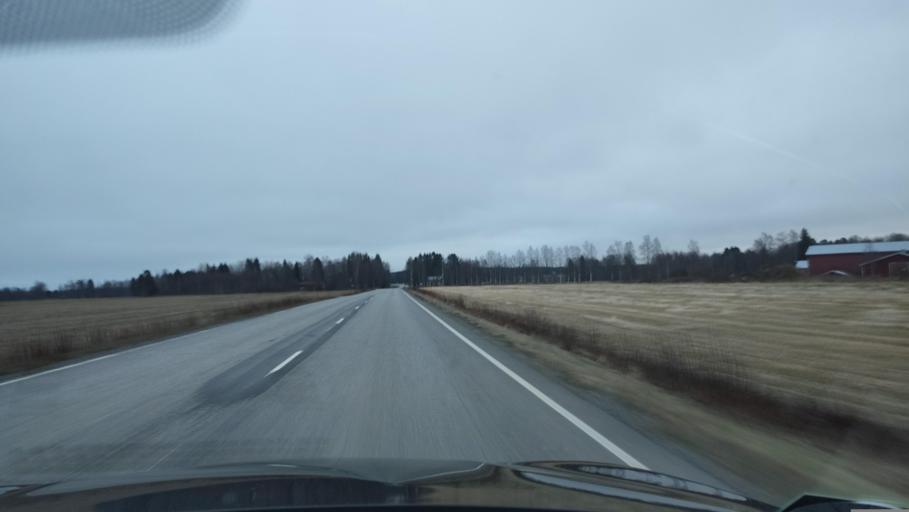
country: FI
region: Southern Ostrobothnia
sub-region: Suupohja
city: Kauhajoki
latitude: 62.3460
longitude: 22.0300
